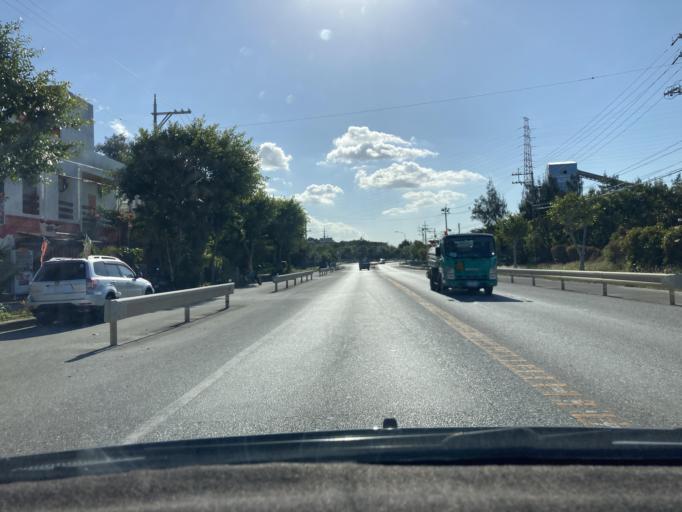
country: JP
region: Okinawa
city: Ishikawa
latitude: 26.4370
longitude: 127.8420
